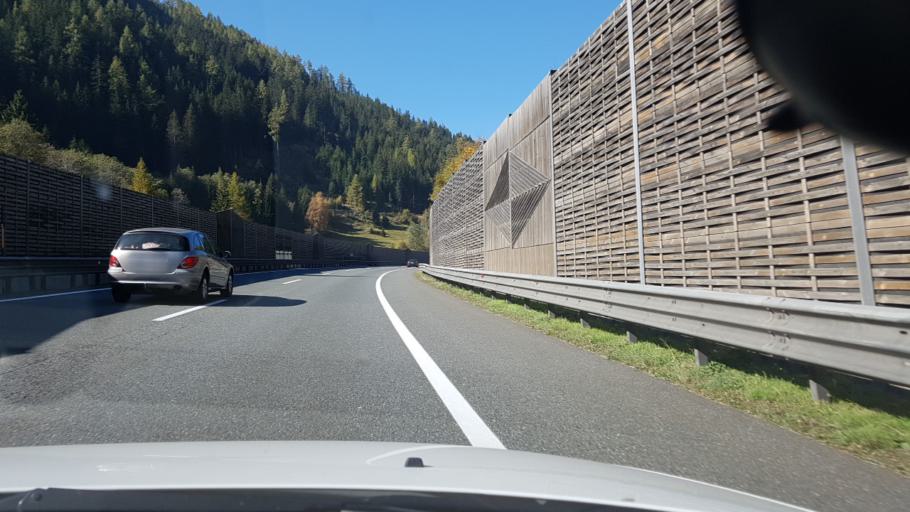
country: AT
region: Salzburg
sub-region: Politischer Bezirk Tamsweg
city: Zederhaus
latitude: 47.1637
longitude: 13.4712
